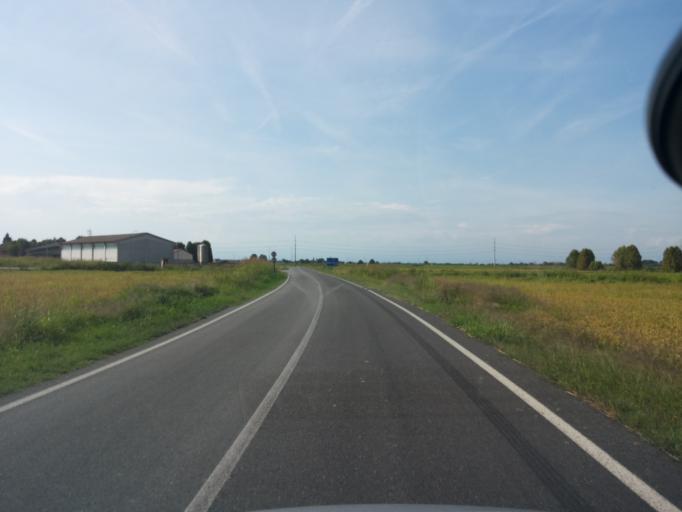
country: IT
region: Piedmont
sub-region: Provincia di Vercelli
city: Desana
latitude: 45.2727
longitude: 8.3660
